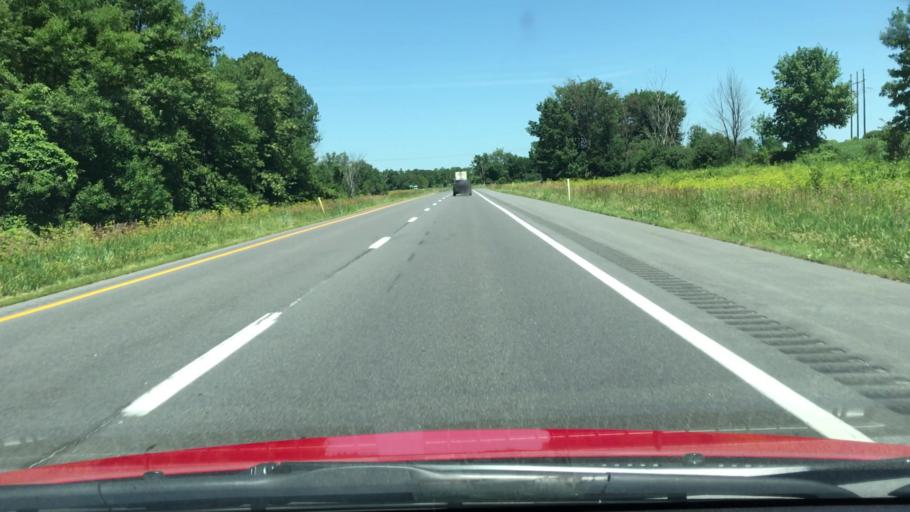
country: US
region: New York
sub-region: Clinton County
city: Cumberland Head
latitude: 44.7405
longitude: -73.4308
